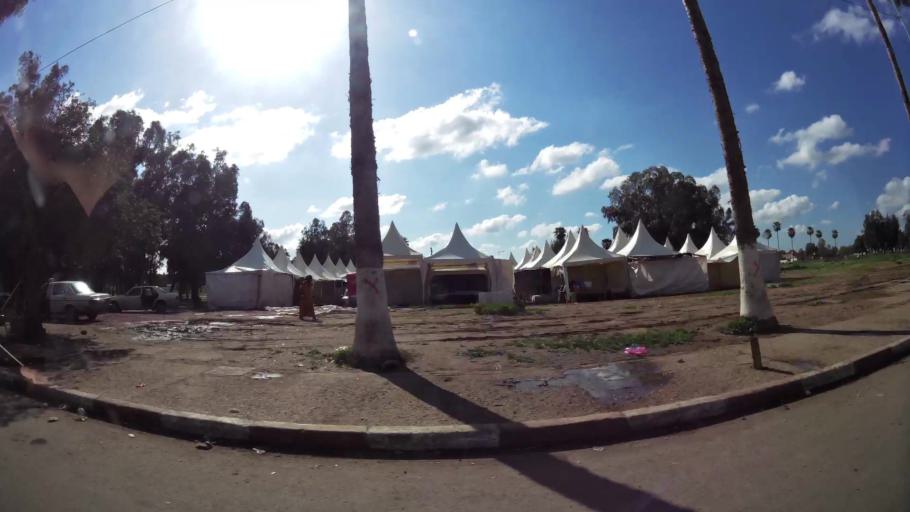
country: MA
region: Chaouia-Ouardigha
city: Nouaseur
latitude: 33.3729
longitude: -7.5421
